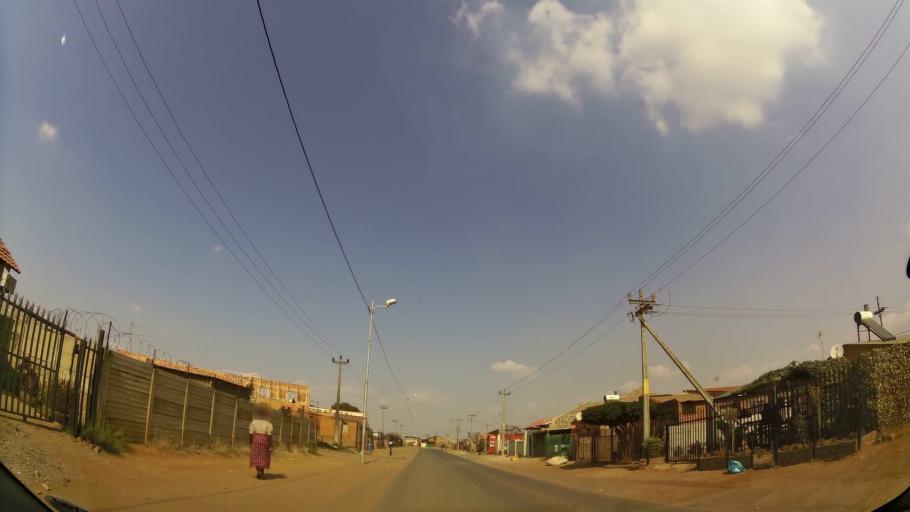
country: ZA
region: Gauteng
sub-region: Ekurhuleni Metropolitan Municipality
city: Springs
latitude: -26.1187
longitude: 28.4840
